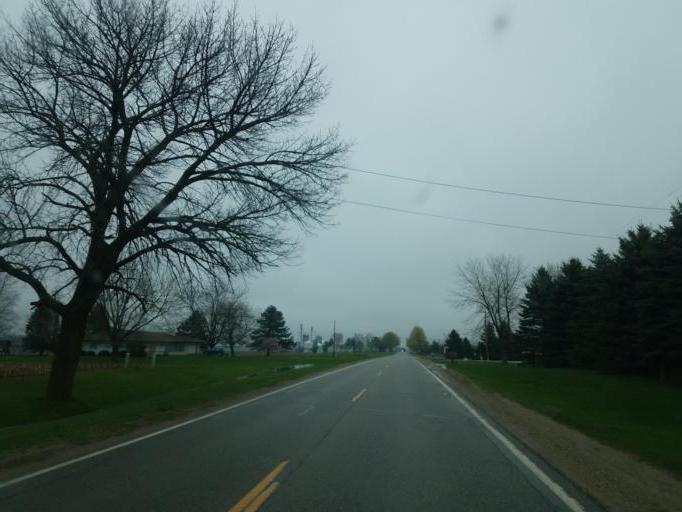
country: US
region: Michigan
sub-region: Isabella County
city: Shepherd
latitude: 43.5242
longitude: -84.7479
